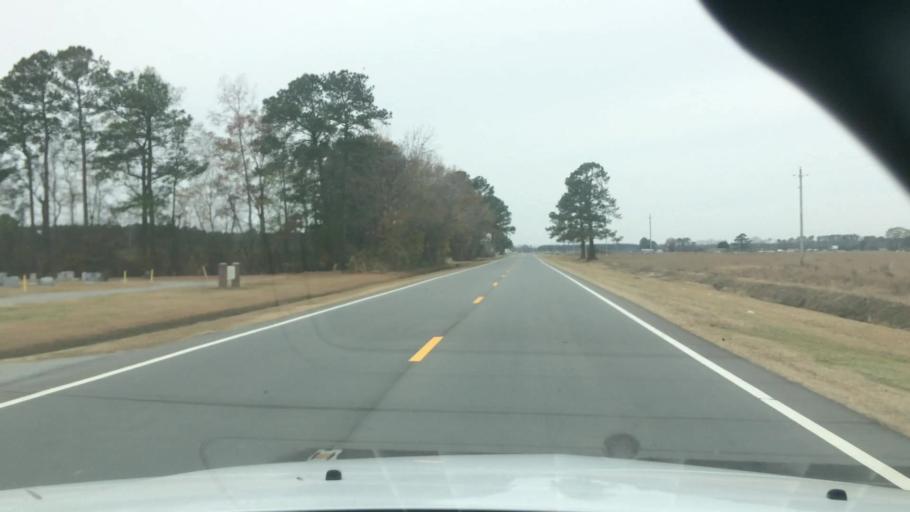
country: US
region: North Carolina
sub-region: Pitt County
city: Farmville
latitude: 35.6002
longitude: -77.6401
